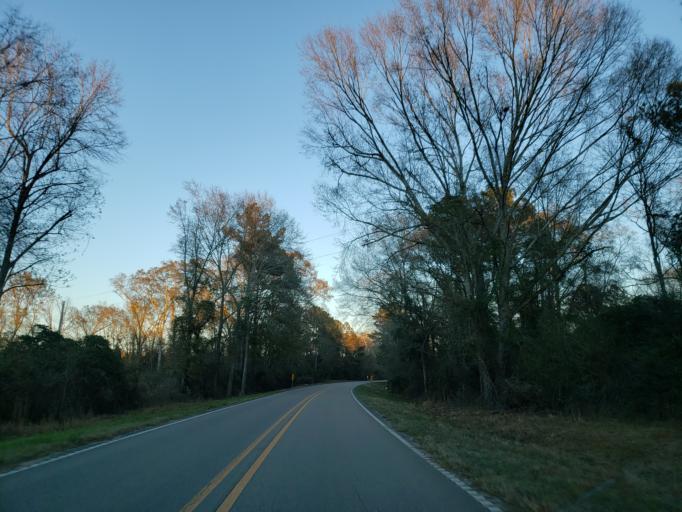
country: US
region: Mississippi
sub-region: Covington County
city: Collins
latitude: 31.5640
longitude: -89.4393
